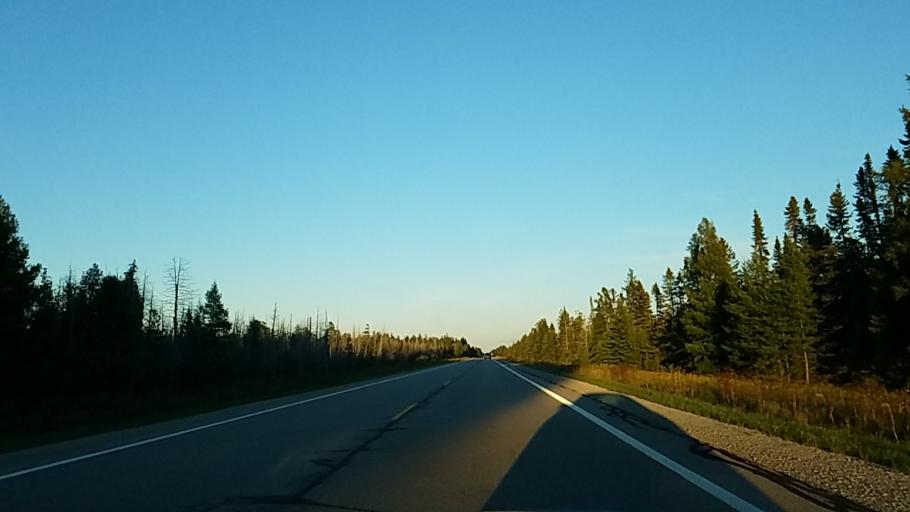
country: US
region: Michigan
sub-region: Alger County
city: Munising
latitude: 46.3467
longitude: -86.3775
